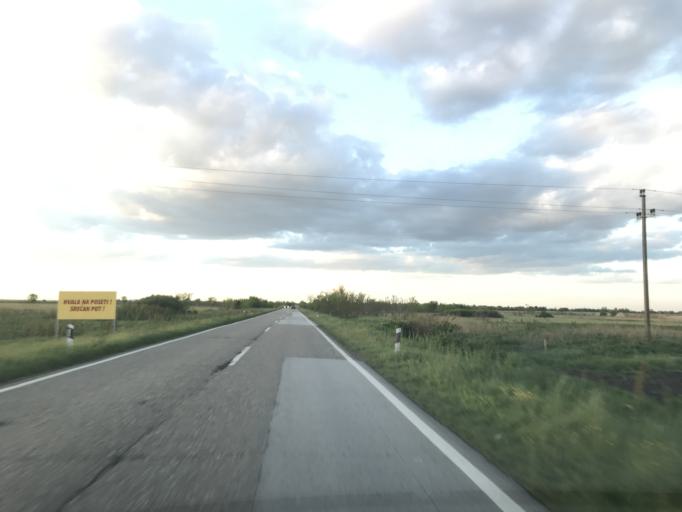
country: RS
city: Cestereg
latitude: 45.5721
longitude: 20.5418
